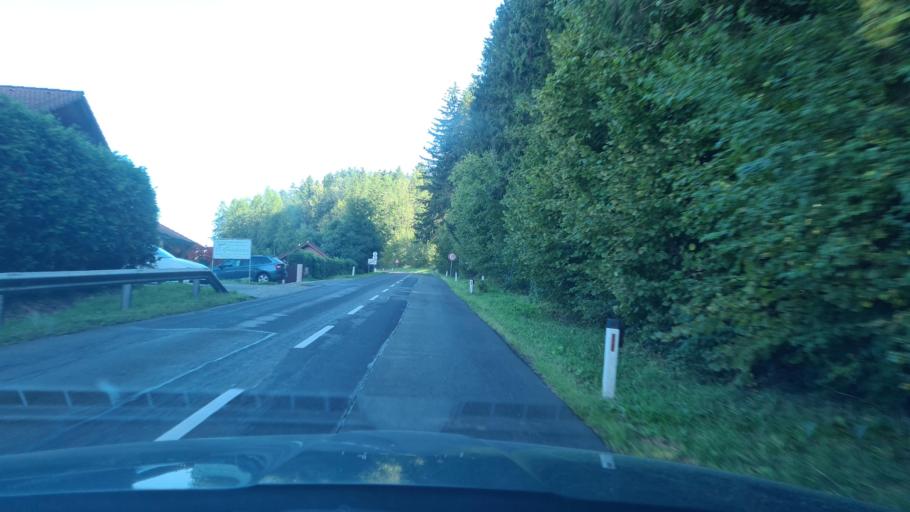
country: AT
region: Styria
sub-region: Politischer Bezirk Leoben
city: Trofaiach
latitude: 47.4040
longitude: 15.0005
